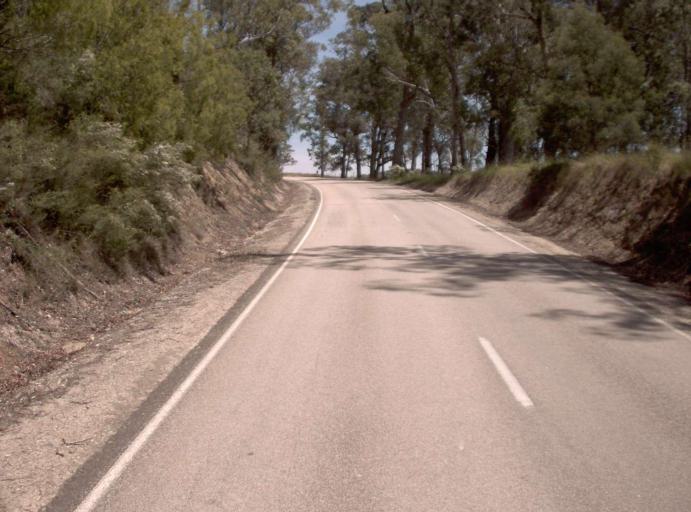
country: AU
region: Victoria
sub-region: East Gippsland
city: Lakes Entrance
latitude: -37.6732
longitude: 147.8593
